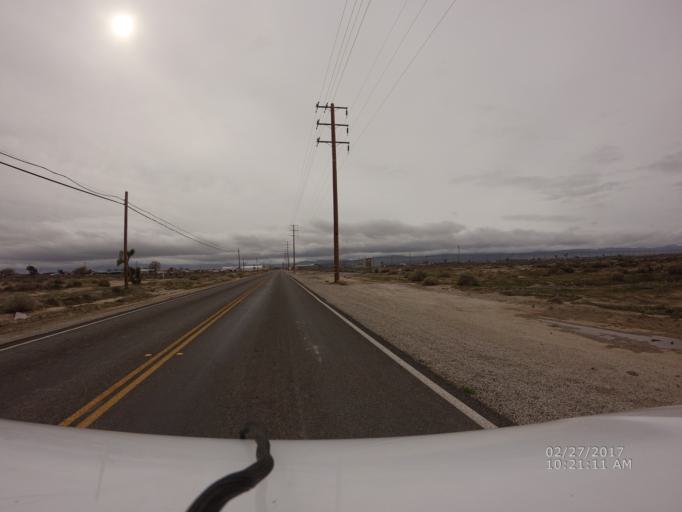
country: US
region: California
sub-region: Los Angeles County
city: Lancaster
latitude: 34.7290
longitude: -118.1308
